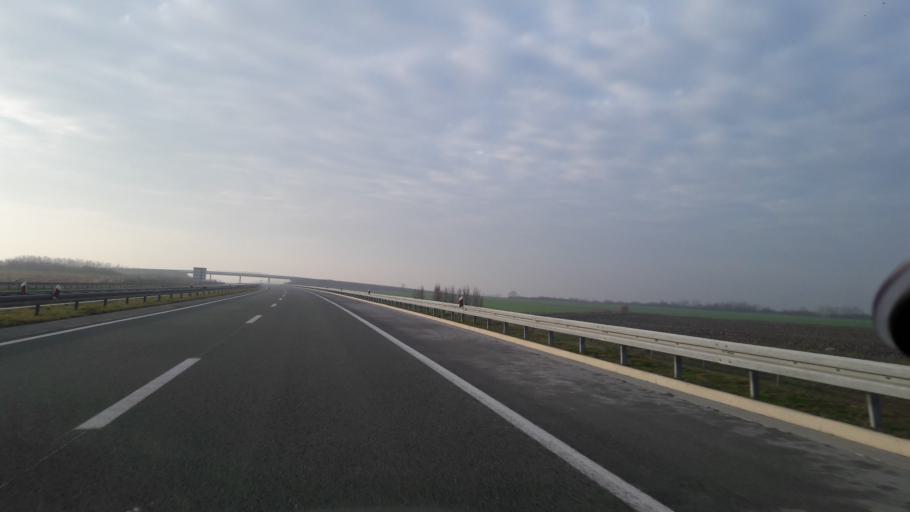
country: HR
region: Osjecko-Baranjska
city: Gorjani
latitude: 45.3834
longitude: 18.3963
